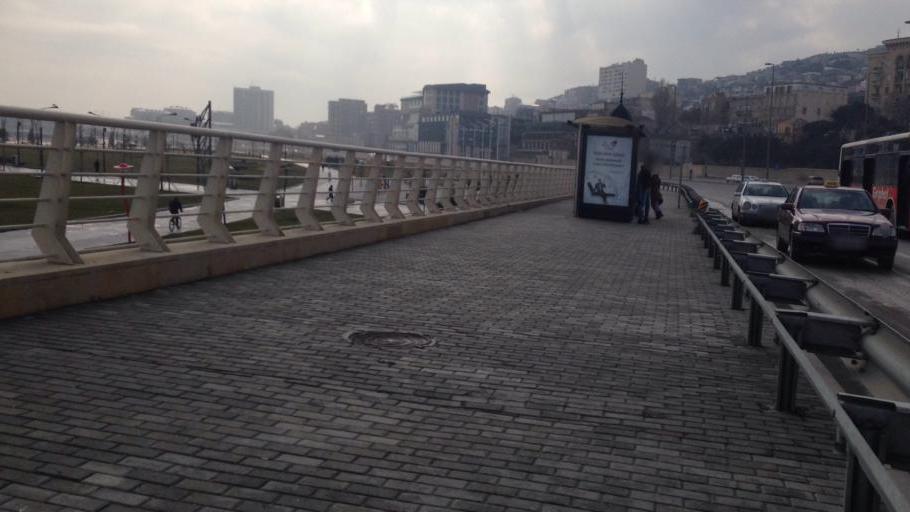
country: AZ
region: Baki
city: Badamdar
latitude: 40.3531
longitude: 49.8346
